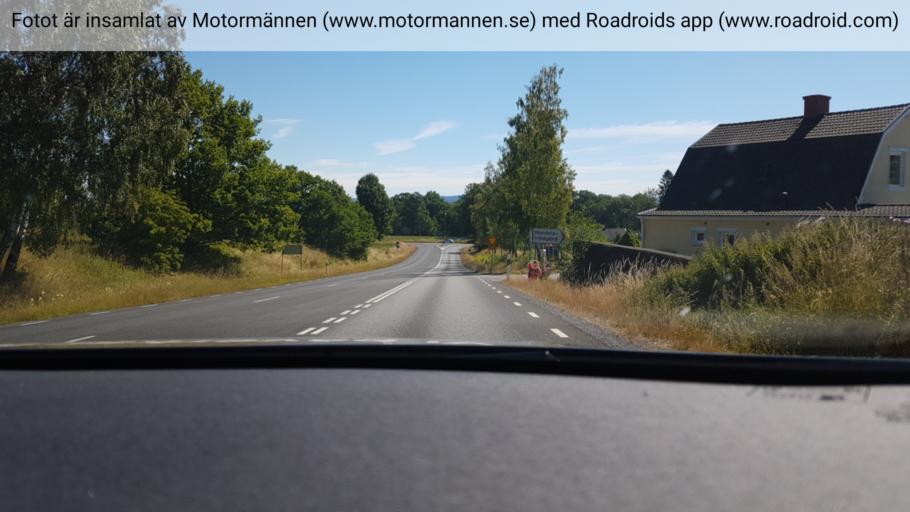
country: SE
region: Joenkoeping
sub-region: Jonkopings Kommun
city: Jonkoping
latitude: 57.8154
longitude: 14.1418
